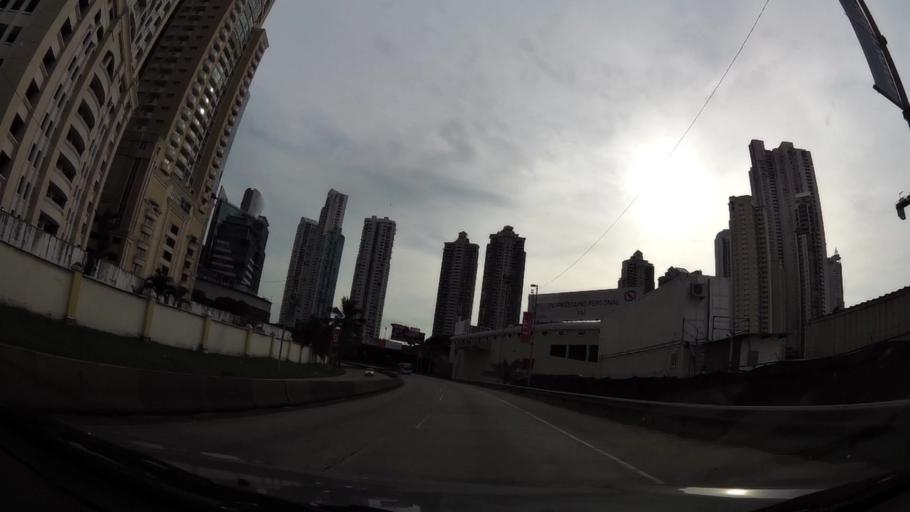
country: PA
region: Panama
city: Panama
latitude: 8.9788
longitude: -79.5113
